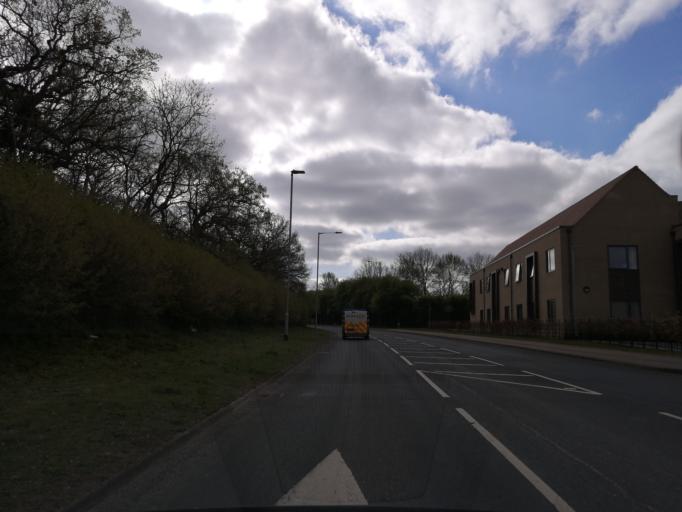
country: GB
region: England
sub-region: Peterborough
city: Marholm
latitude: 52.5686
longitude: -0.2943
